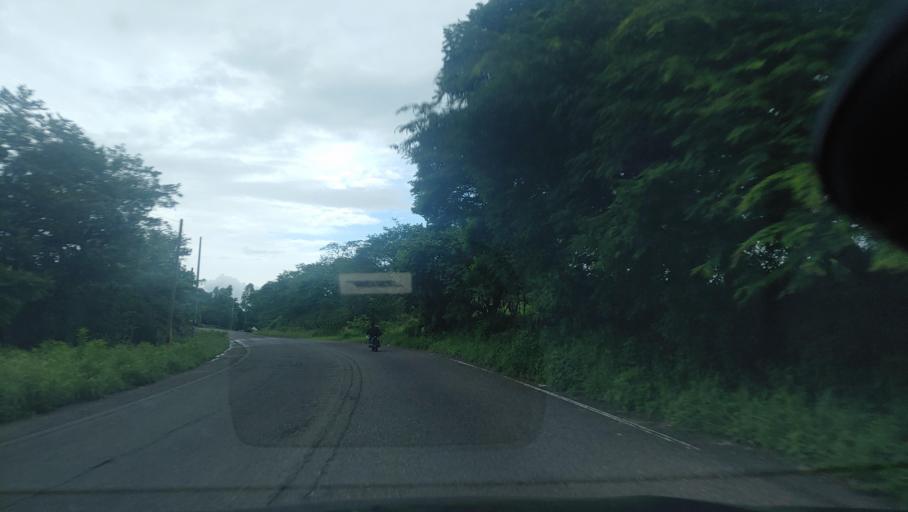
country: HN
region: Choluteca
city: Corpus
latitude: 13.3660
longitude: -86.9953
